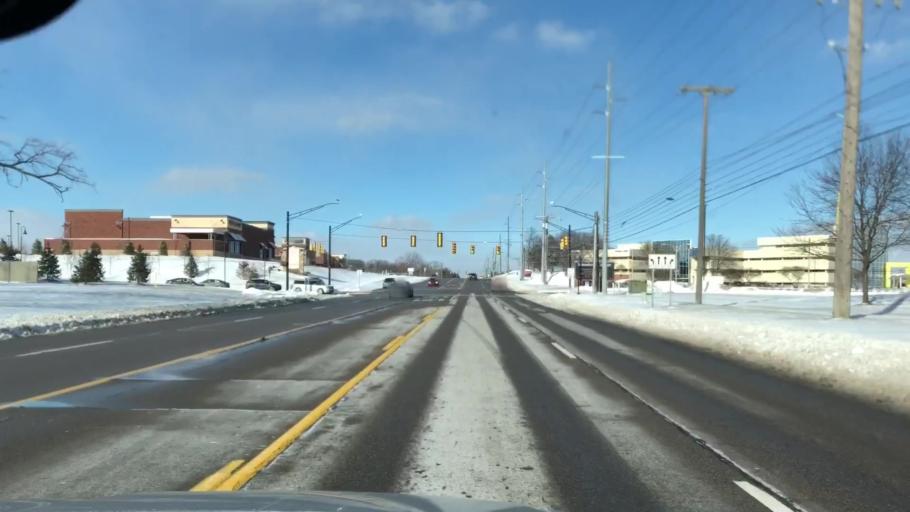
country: US
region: Michigan
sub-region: Wayne County
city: Northville
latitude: 42.4213
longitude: -83.4328
